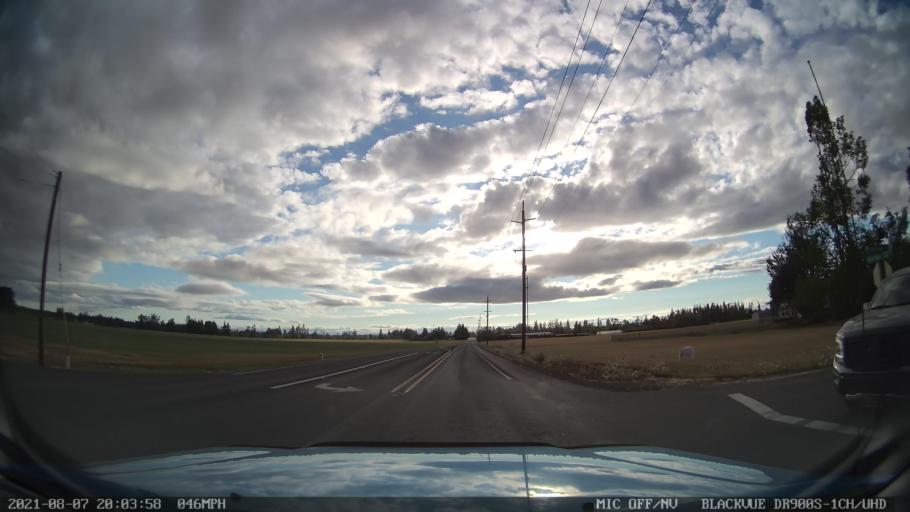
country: US
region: Oregon
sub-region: Marion County
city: Silverton
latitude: 44.9944
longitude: -122.8245
